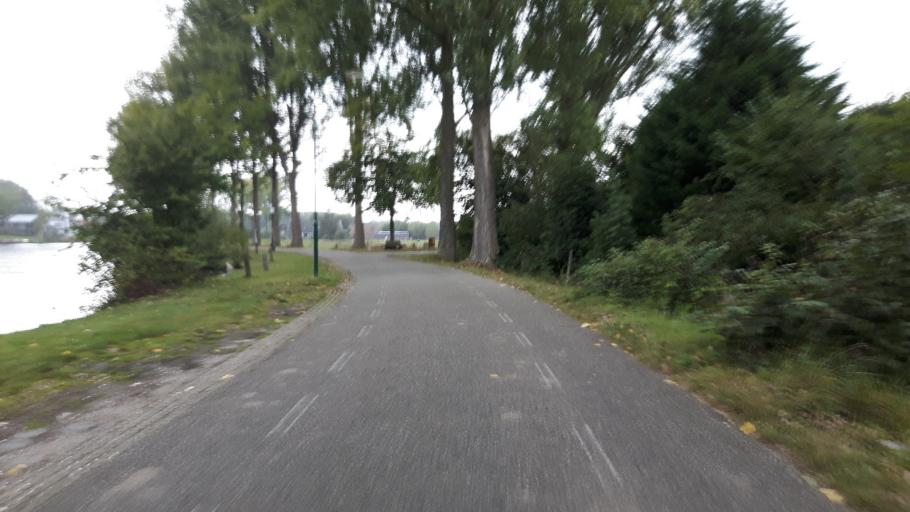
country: NL
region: Utrecht
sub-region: Stichtse Vecht
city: Maarssen
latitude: 52.1310
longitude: 5.0682
